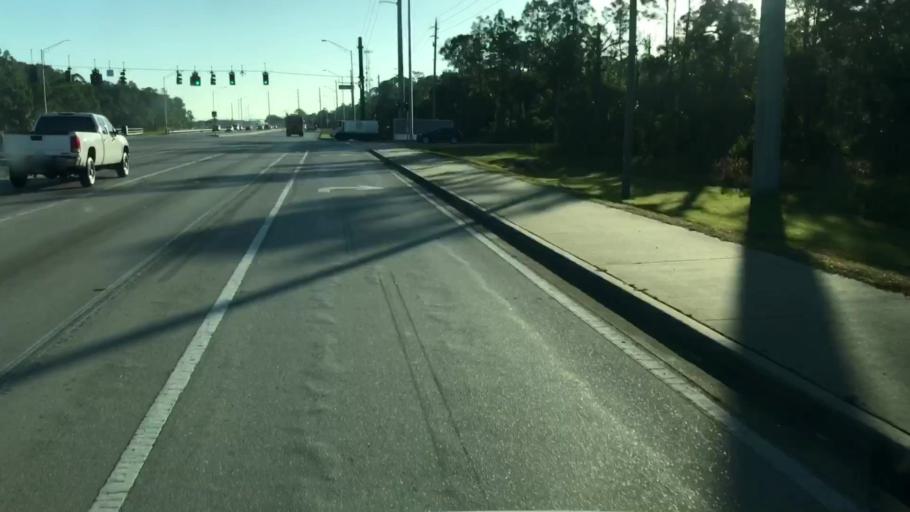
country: US
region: Florida
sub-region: Collier County
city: Orangetree
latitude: 26.2763
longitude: -81.6081
